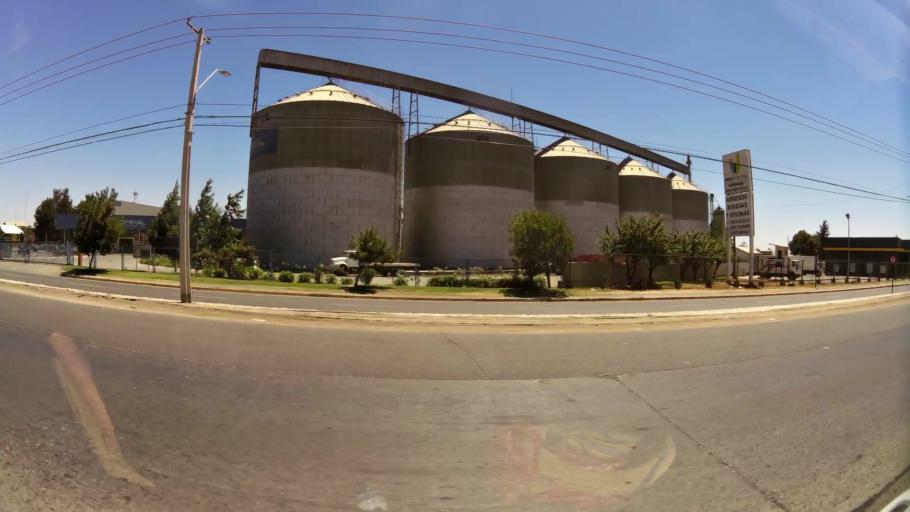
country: CL
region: O'Higgins
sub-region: Provincia de Cachapoal
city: Rancagua
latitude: -34.1865
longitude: -70.7434
